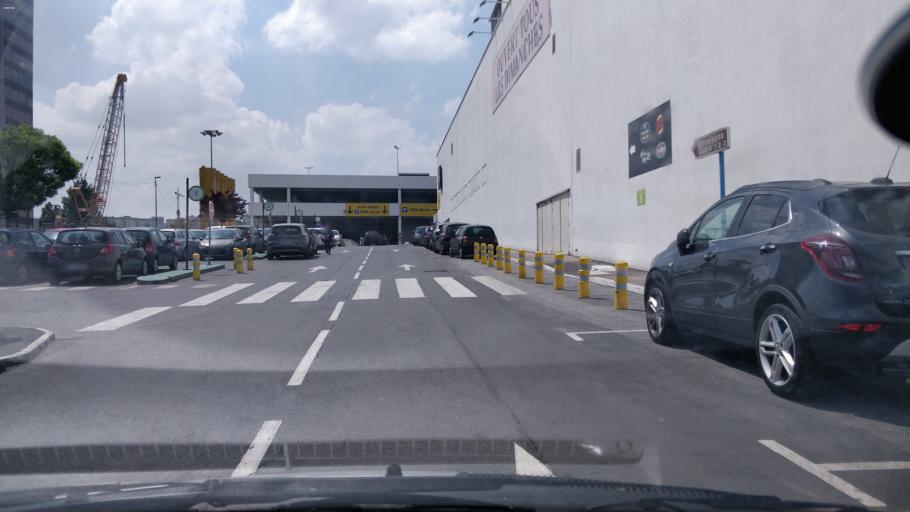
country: FR
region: Ile-de-France
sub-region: Departement de Seine-Saint-Denis
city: Noisy-le-Sec
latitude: 48.8815
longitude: 2.4799
